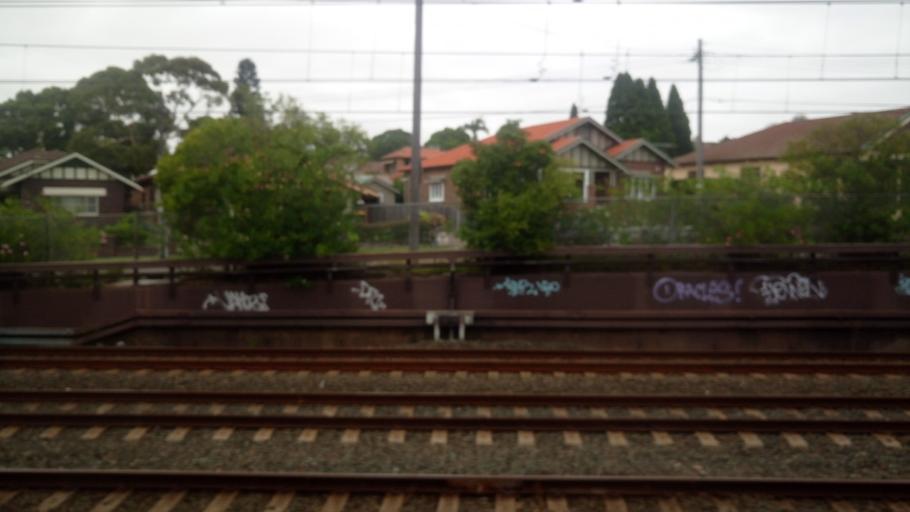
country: AU
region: New South Wales
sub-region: Ashfield
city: Croydon
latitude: -33.8796
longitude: 151.1106
